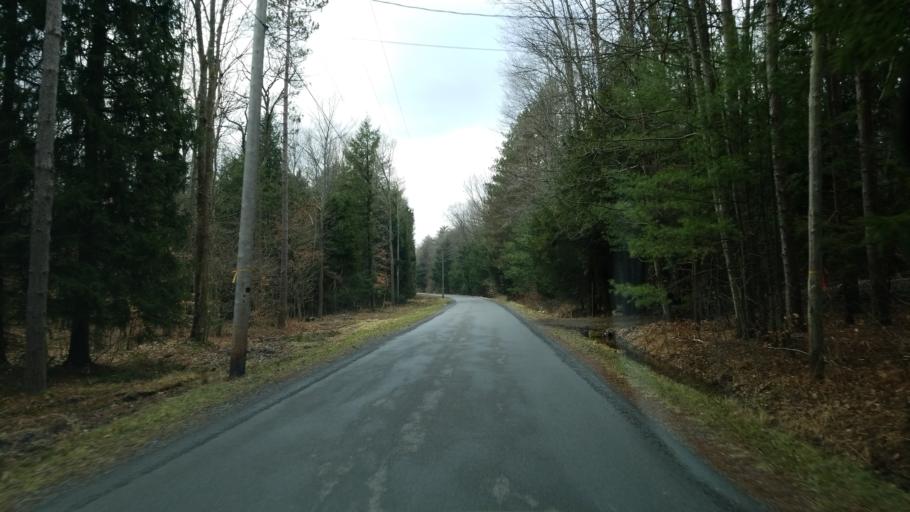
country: US
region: Pennsylvania
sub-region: Clearfield County
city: Treasure Lake
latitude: 41.1477
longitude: -78.5627
